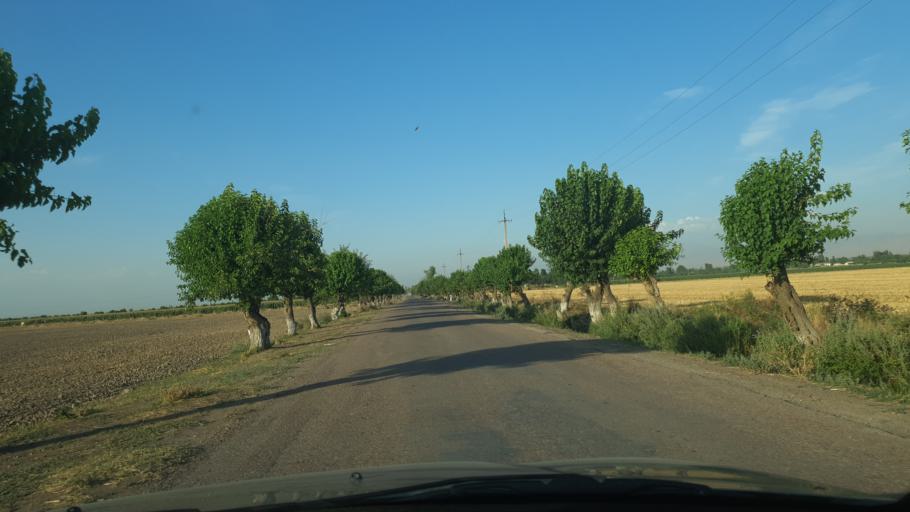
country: UZ
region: Toshkent
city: Tuytepa
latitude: 41.0997
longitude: 69.3801
